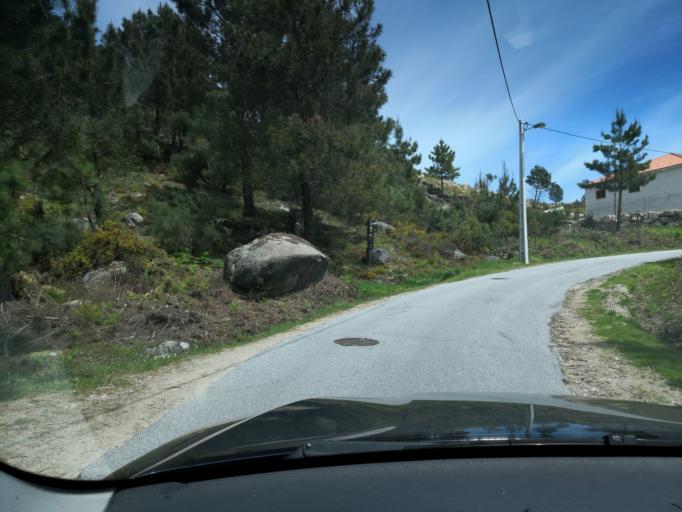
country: PT
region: Vila Real
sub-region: Vila Real
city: Vila Real
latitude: 41.3224
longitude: -7.7923
